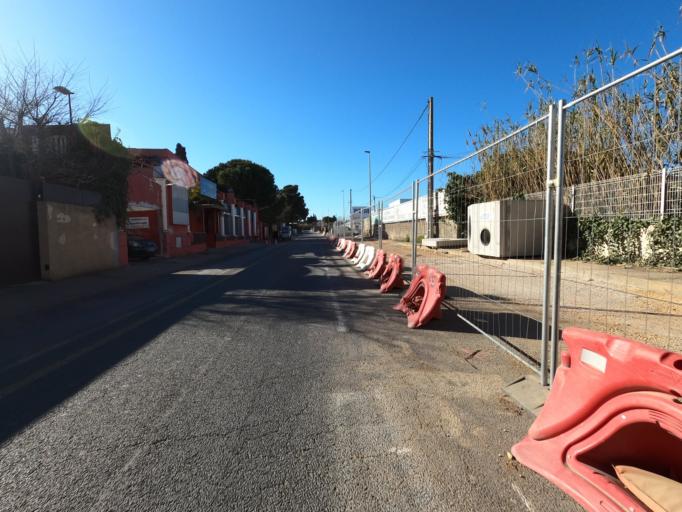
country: FR
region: Languedoc-Roussillon
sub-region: Departement de l'Herault
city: Montpellier
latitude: 43.5824
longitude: 3.8793
